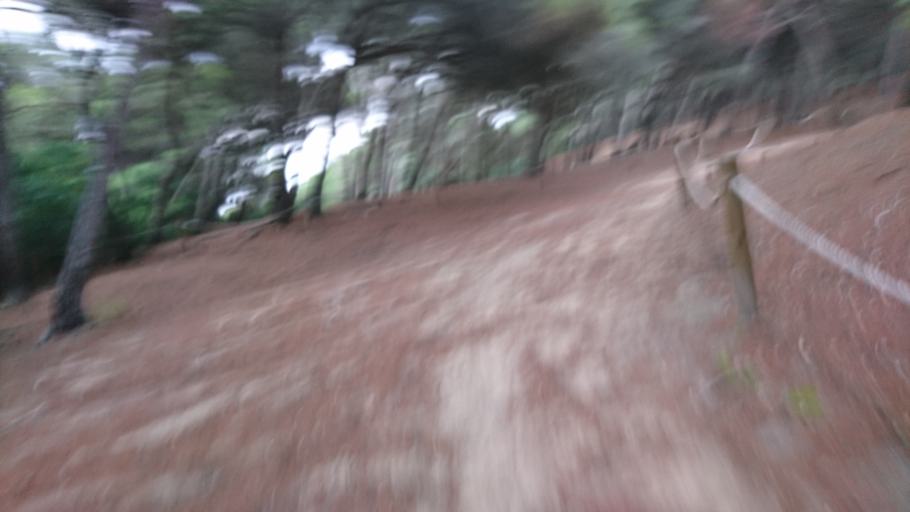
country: ES
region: Balearic Islands
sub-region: Illes Balears
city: Port d'Alcudia
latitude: 39.7804
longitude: 3.1345
